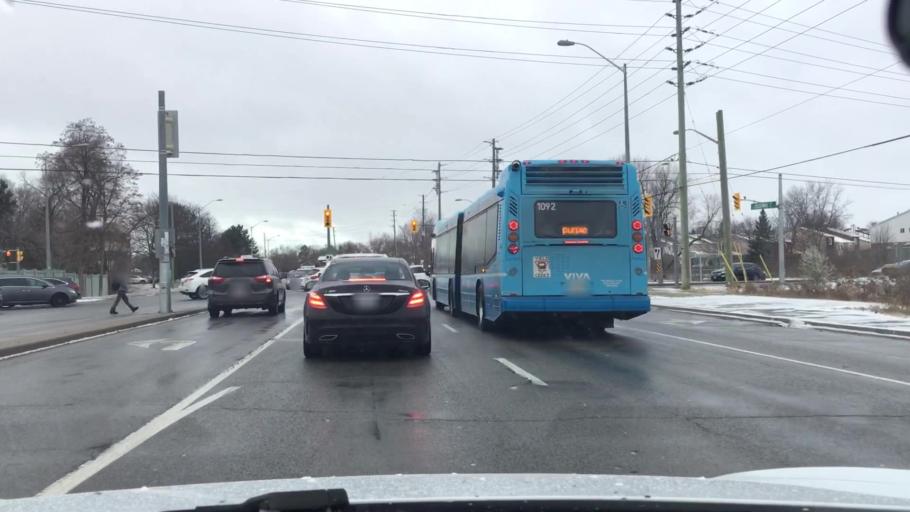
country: CA
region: Ontario
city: Markham
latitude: 43.8788
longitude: -79.2343
